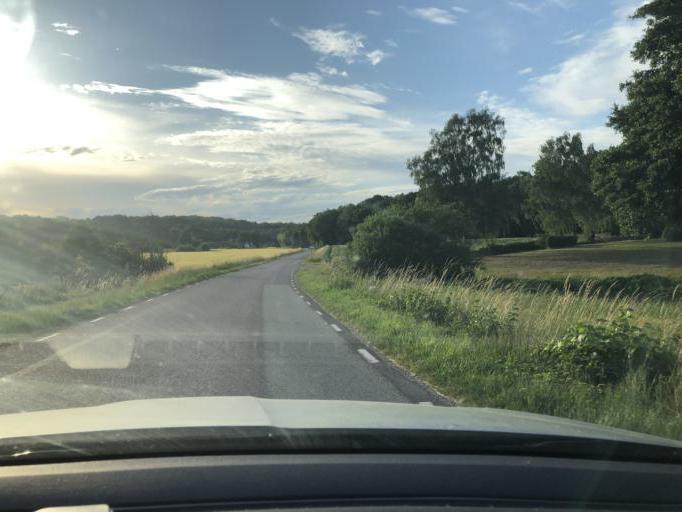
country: SE
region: Blekinge
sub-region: Solvesborgs Kommun
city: Soelvesborg
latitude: 56.1243
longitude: 14.6132
